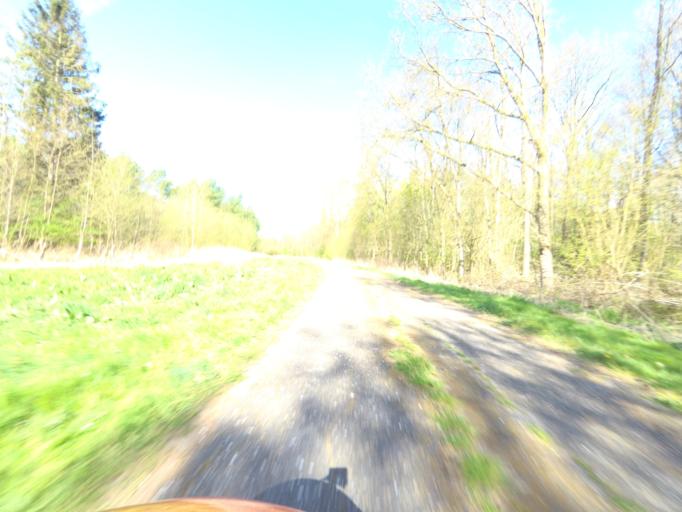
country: NL
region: Flevoland
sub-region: Gemeente Lelystad
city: Lelystad
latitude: 52.4439
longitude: 5.5683
